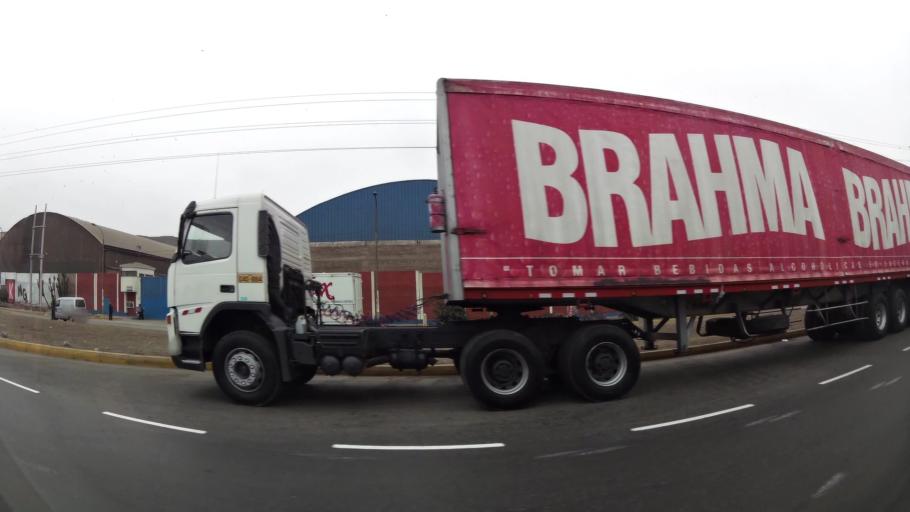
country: PE
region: Lima
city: Ventanilla
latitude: -11.9474
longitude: -77.1316
